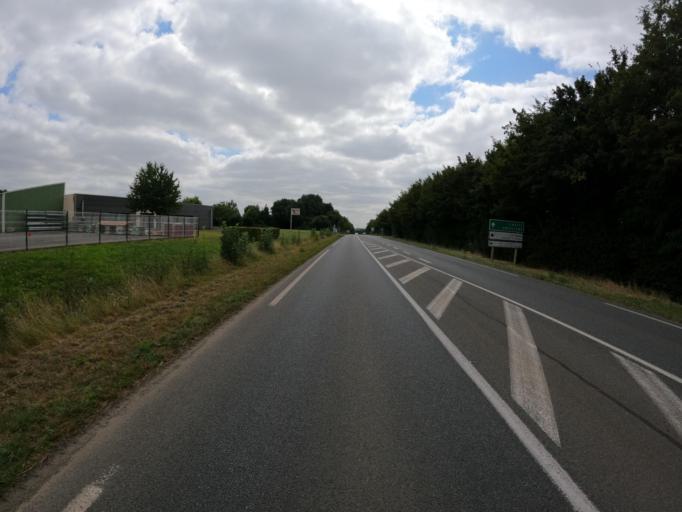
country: FR
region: Poitou-Charentes
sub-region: Departement des Deux-Sevres
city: Melle
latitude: 46.2213
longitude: -0.1556
